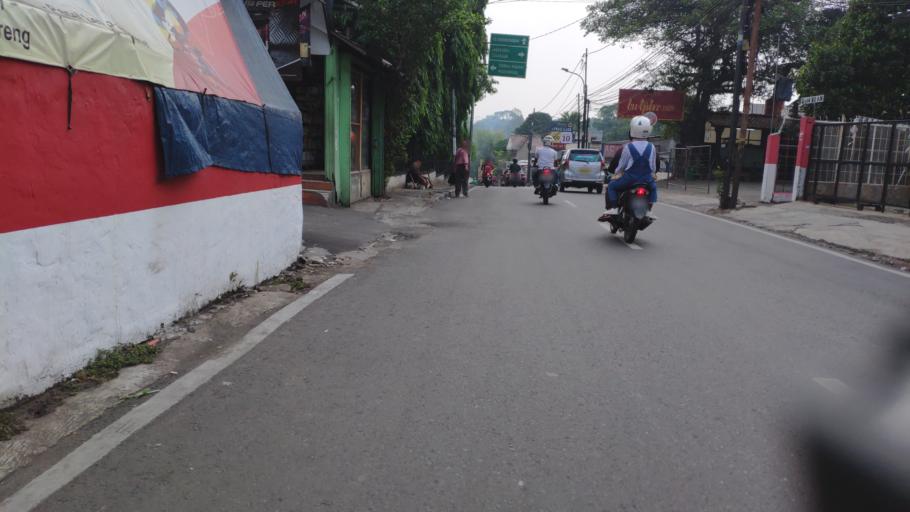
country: ID
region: West Java
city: Pamulang
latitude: -6.3108
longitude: 106.8143
